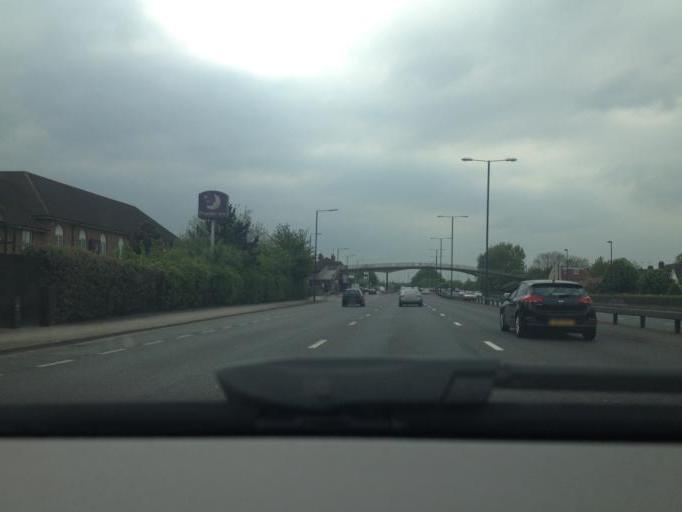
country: GB
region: England
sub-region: Greater London
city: Ealing Broadway
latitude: 51.5332
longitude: -0.3213
